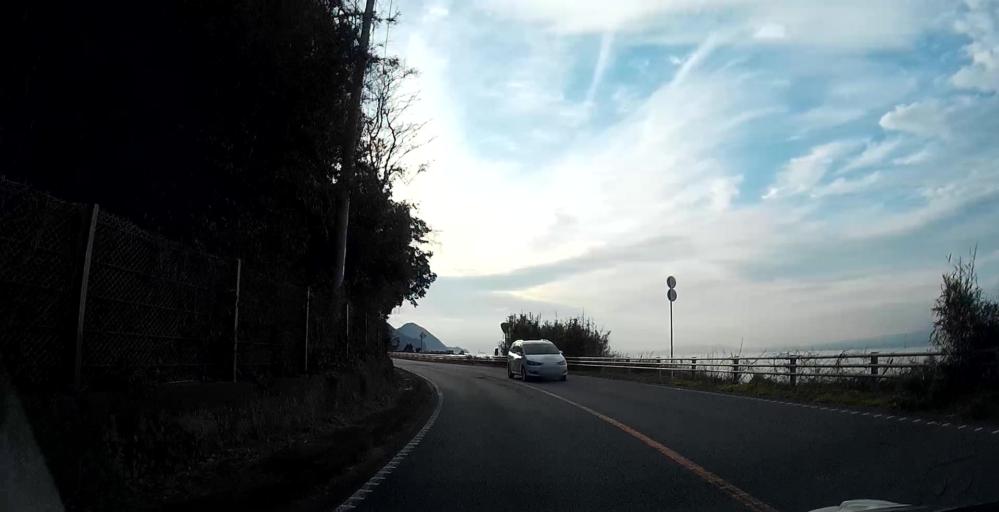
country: JP
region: Nagasaki
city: Shimabara
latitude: 32.6446
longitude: 130.4830
